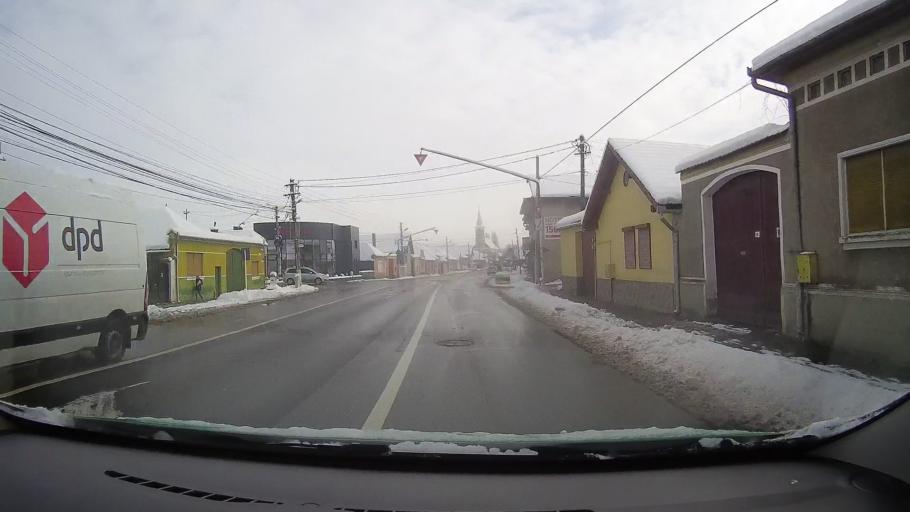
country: RO
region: Alba
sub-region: Municipiul Sebes
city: Sebes
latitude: 45.9594
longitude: 23.5565
